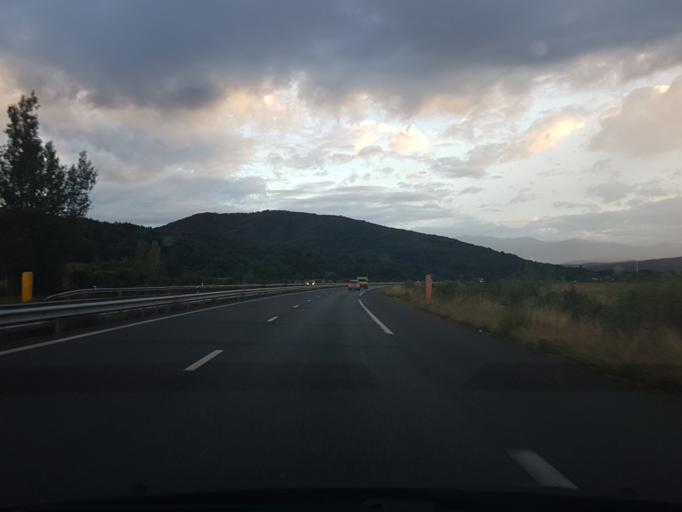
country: FR
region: Midi-Pyrenees
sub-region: Departement de l'Ariege
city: Varilhes
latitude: 43.0481
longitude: 1.6479
